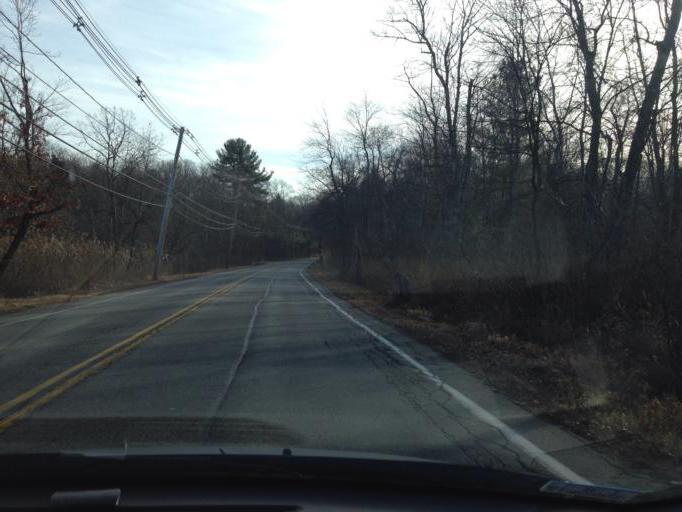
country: US
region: Massachusetts
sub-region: Middlesex County
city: Bedford
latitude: 42.5009
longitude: -71.2954
